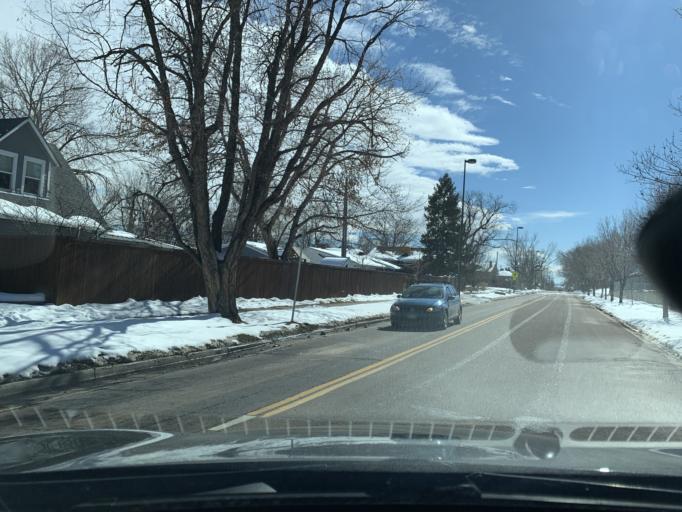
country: US
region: Colorado
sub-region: Adams County
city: Berkley
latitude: 39.7730
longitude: -105.0300
